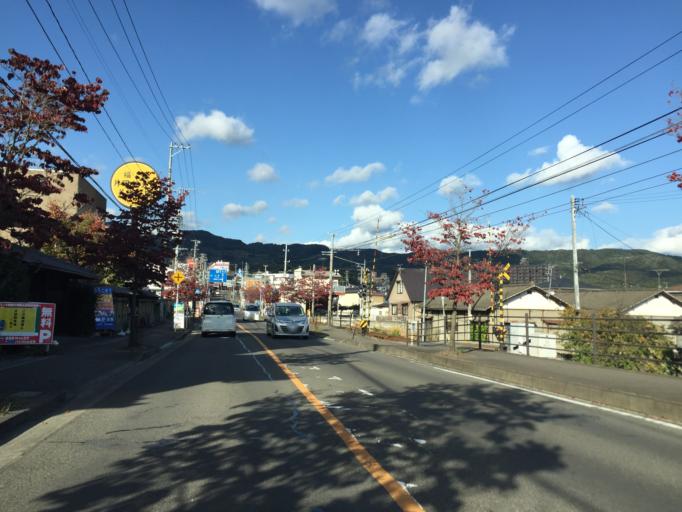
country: JP
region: Fukushima
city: Fukushima-shi
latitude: 37.8259
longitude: 140.4500
